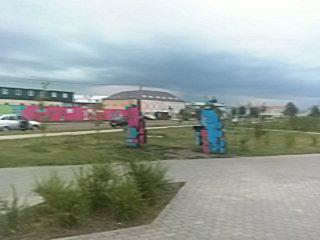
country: RU
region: Tatarstan
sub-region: Tukayevskiy Rayon
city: Naberezhnyye Chelny
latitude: 55.7006
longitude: 52.3147
